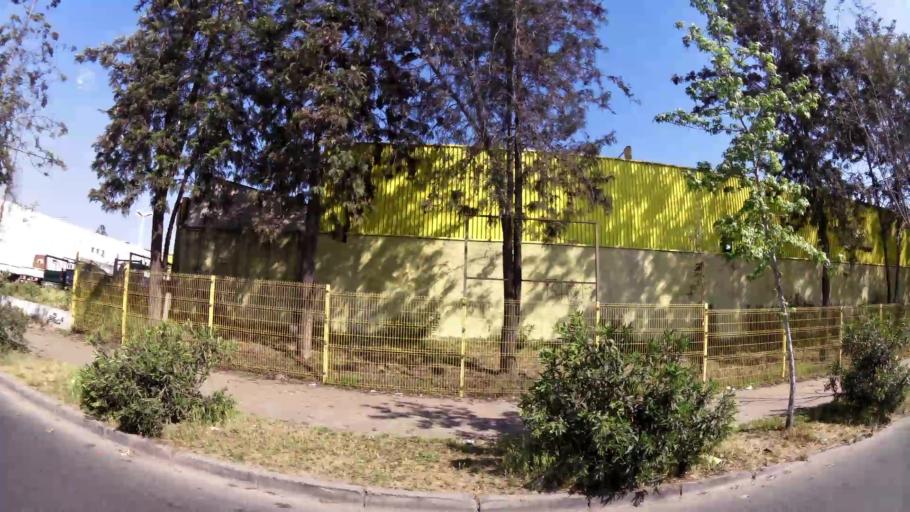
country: CL
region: Santiago Metropolitan
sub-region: Provincia de Santiago
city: La Pintana
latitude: -33.5396
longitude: -70.5922
